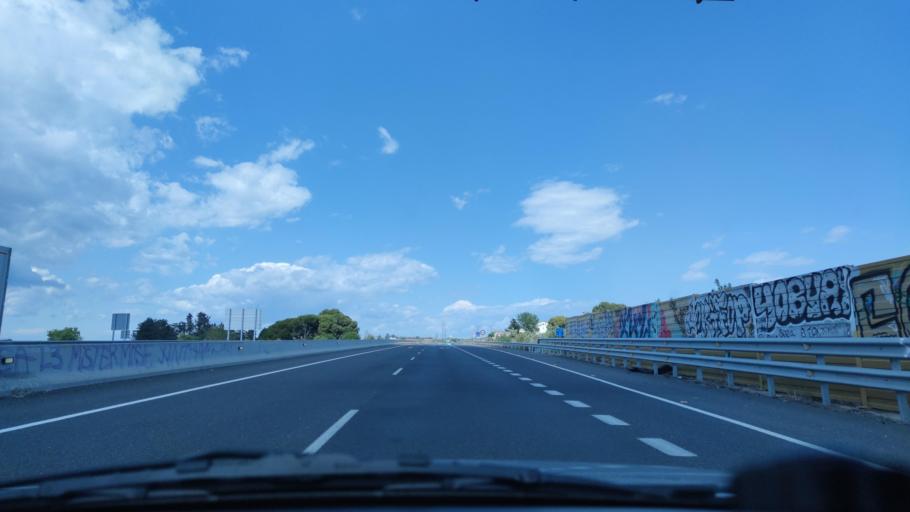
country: ES
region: Catalonia
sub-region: Provincia de Lleida
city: Lleida
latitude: 41.5915
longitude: 0.6415
